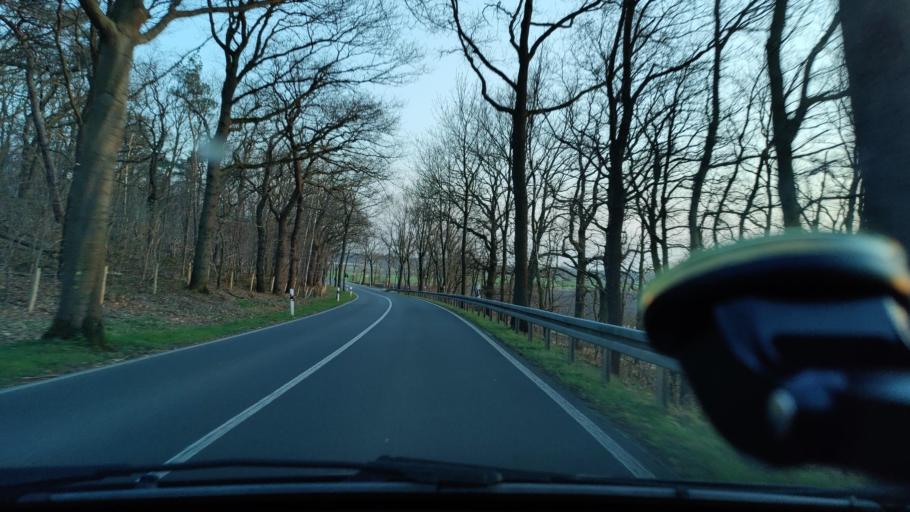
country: NL
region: Limburg
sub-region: Gemeente Bergen
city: Wellerlooi
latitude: 51.6083
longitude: 6.1114
